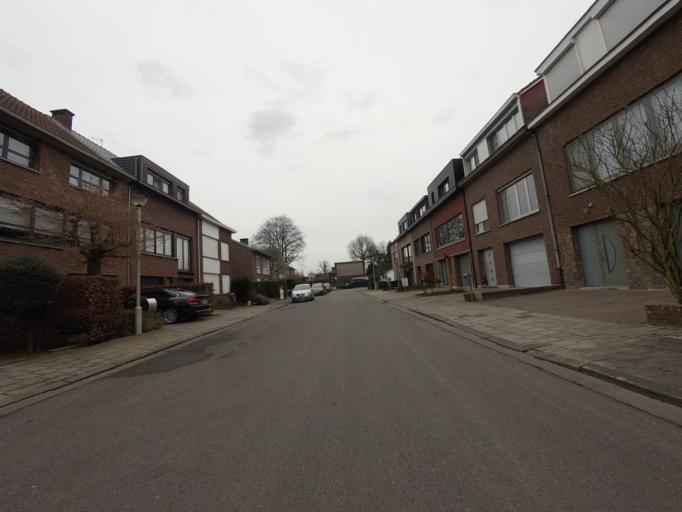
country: BE
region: Flanders
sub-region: Provincie Antwerpen
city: Aartselaar
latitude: 51.1414
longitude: 4.3746
